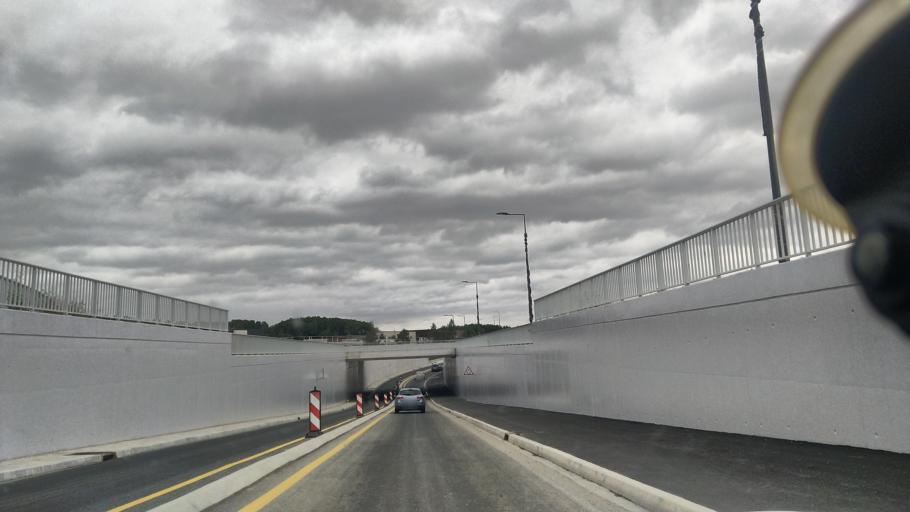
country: FR
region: Ile-de-France
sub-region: Departement de Seine-et-Marne
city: Villevaude
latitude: 48.9418
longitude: 2.6549
